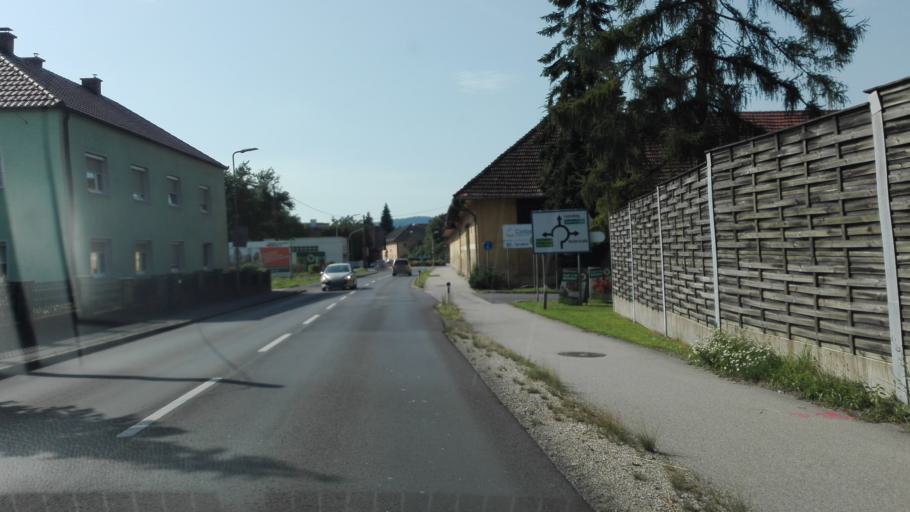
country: AT
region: Upper Austria
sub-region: Politischer Bezirk Linz-Land
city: Leonding
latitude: 48.2628
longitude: 14.2648
